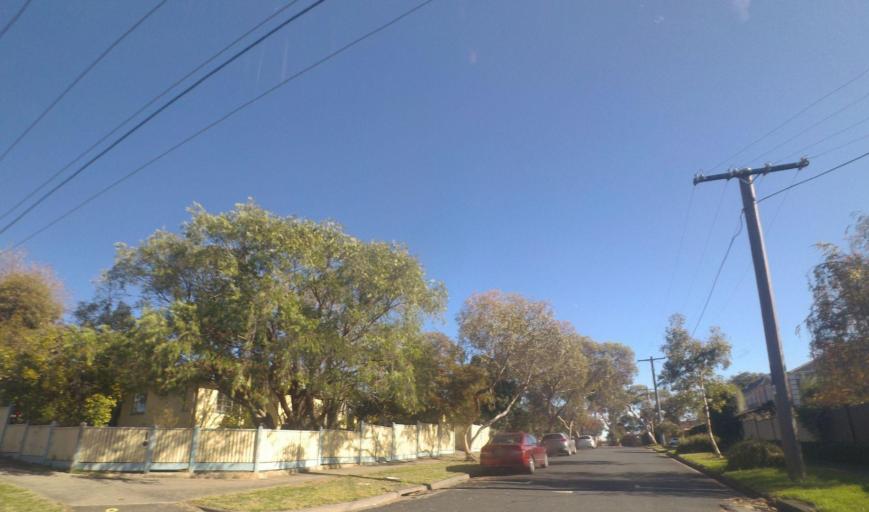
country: AU
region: Victoria
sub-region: Whitehorse
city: Box Hill North
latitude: -37.8070
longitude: 145.1235
